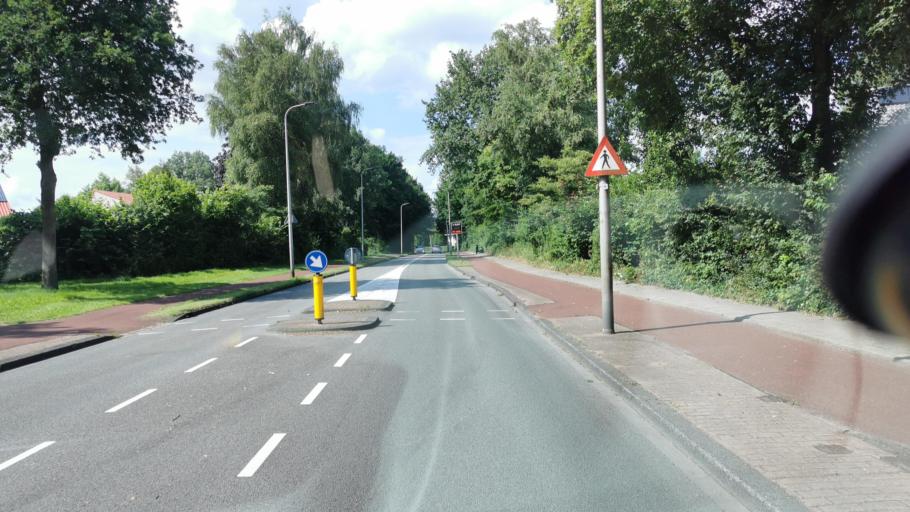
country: NL
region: Overijssel
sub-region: Gemeente Enschede
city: Enschede
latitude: 52.2326
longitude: 6.9233
